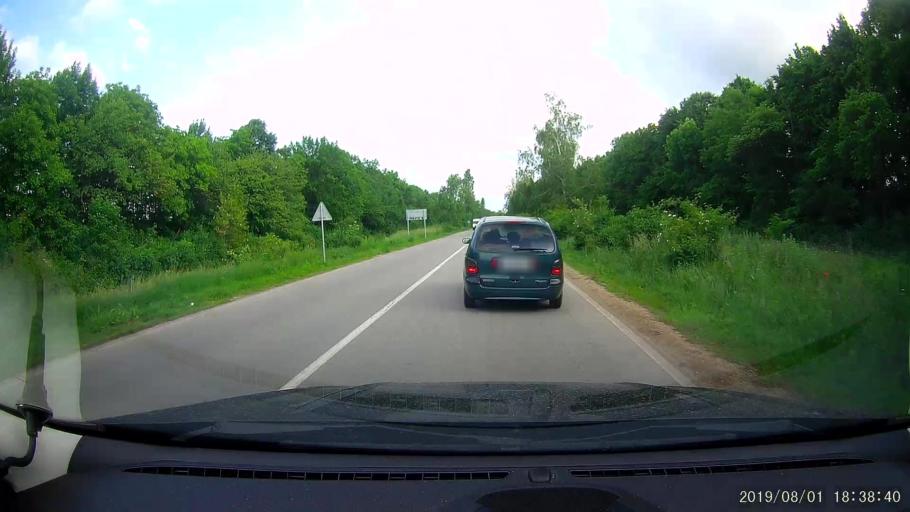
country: BG
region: Shumen
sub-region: Obshtina Khitrino
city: Gara Khitrino
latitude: 43.3991
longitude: 26.9160
